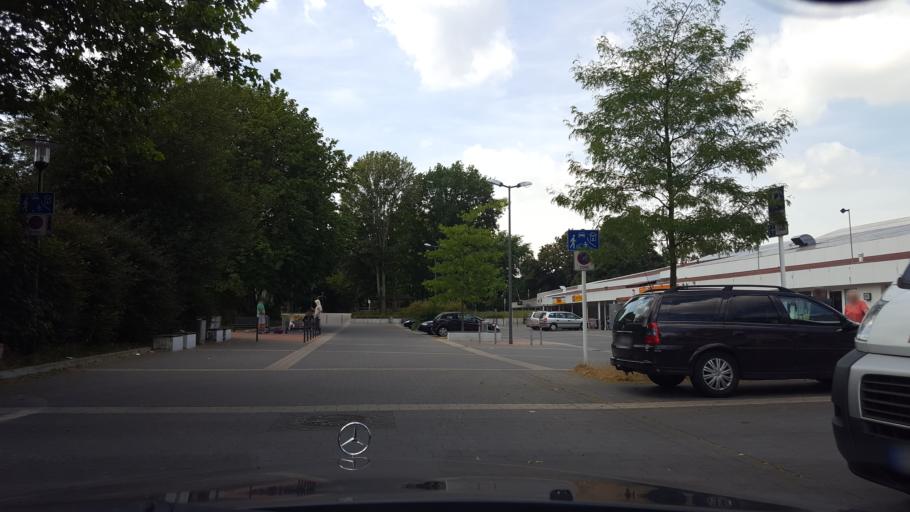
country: DE
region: North Rhine-Westphalia
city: Marl
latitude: 51.6582
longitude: 7.1448
